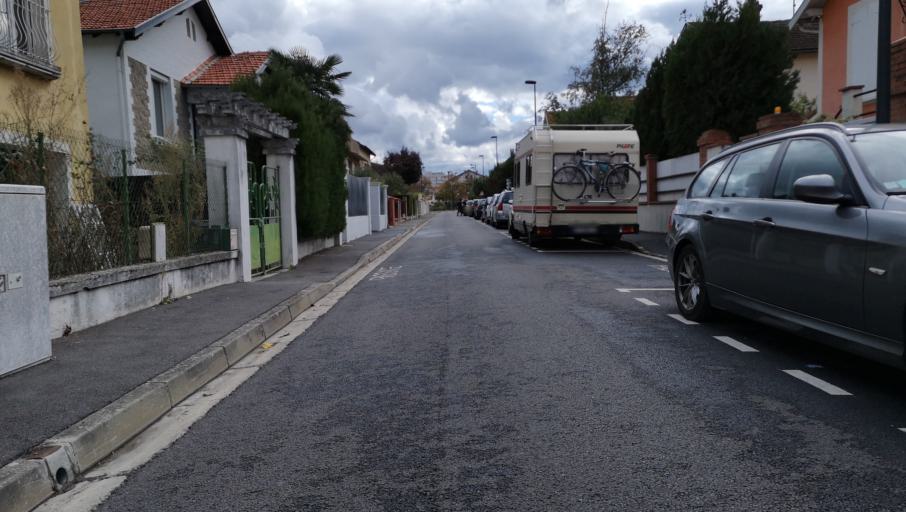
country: FR
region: Midi-Pyrenees
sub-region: Departement de la Haute-Garonne
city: Blagnac
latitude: 43.6073
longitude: 1.4120
